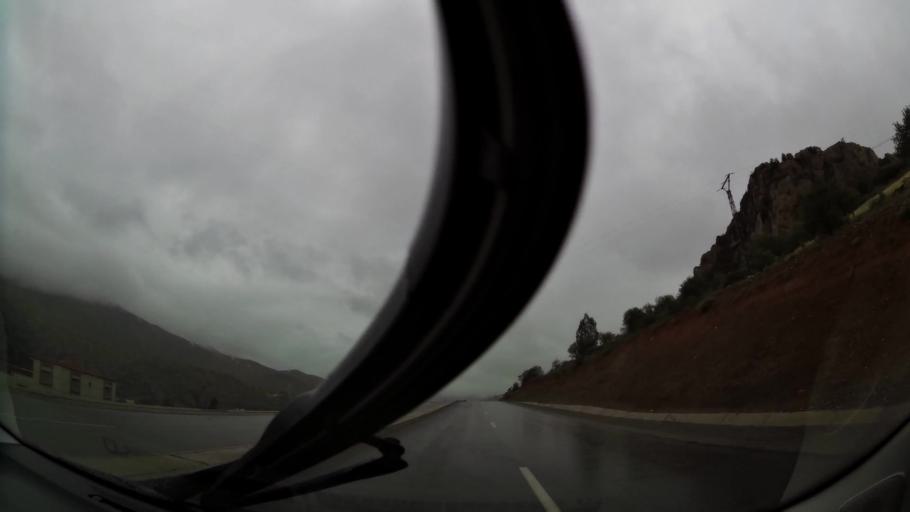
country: MA
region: Taza-Al Hoceima-Taounate
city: Imzourene
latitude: 35.0306
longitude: -3.8213
